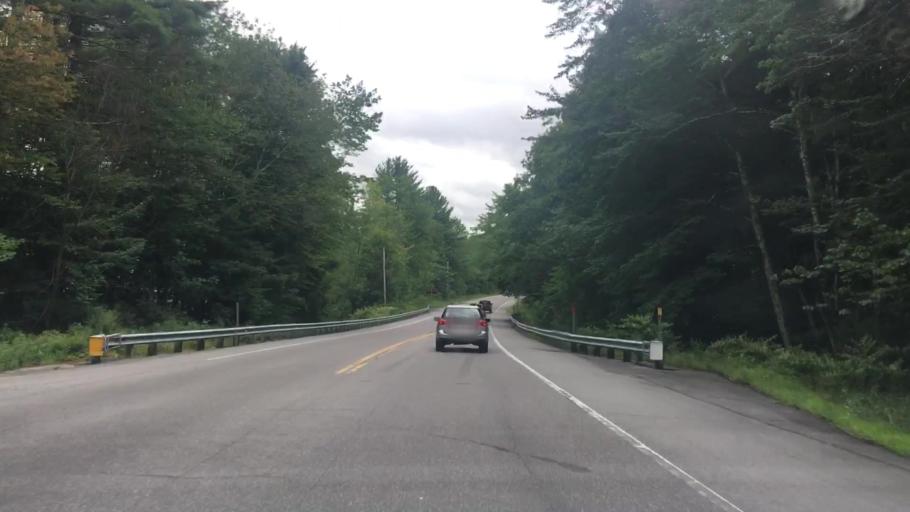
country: US
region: Maine
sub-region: York County
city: Waterboro
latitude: 43.5112
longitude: -70.7169
